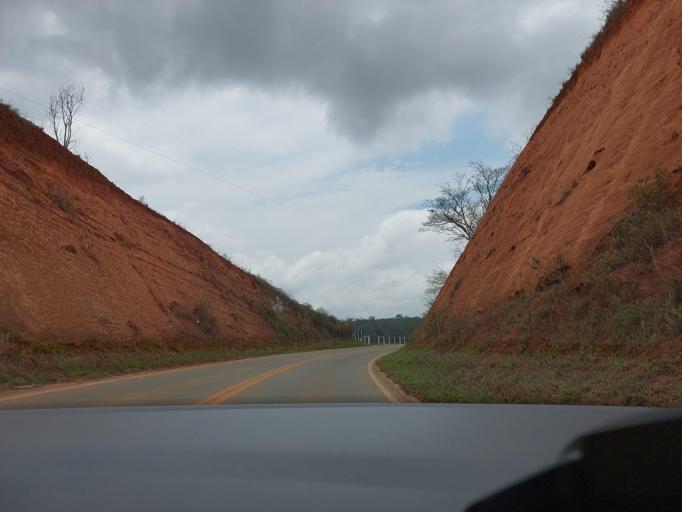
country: BR
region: Minas Gerais
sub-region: Ponte Nova
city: Ponte Nova
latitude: -20.3848
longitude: -42.8722
